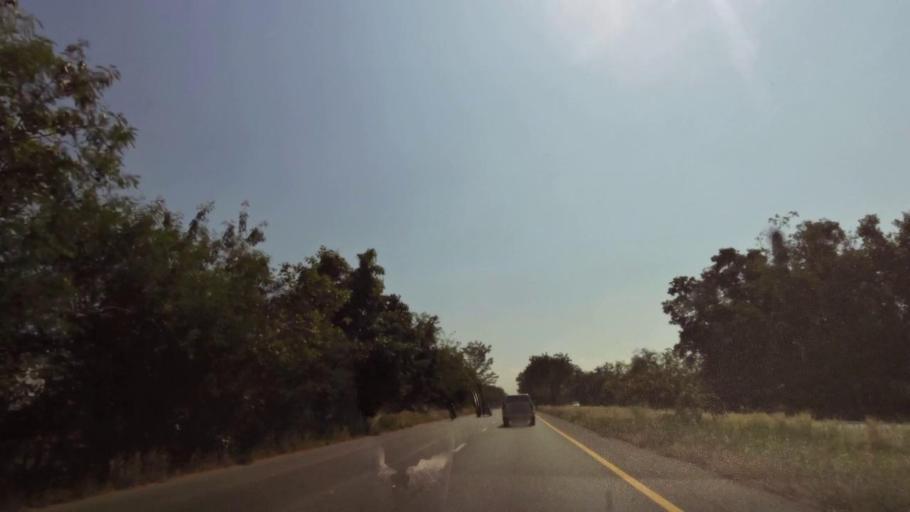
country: TH
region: Nakhon Sawan
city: Kao Liao
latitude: 15.8526
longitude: 100.1172
